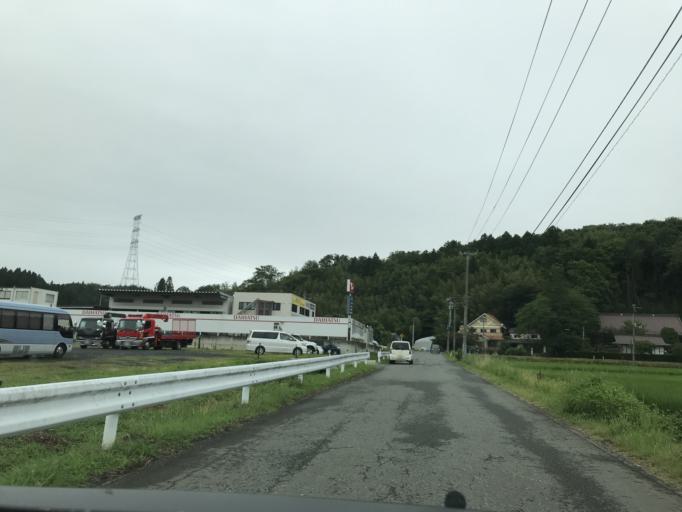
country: JP
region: Iwate
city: Ichinoseki
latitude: 38.8609
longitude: 141.1535
